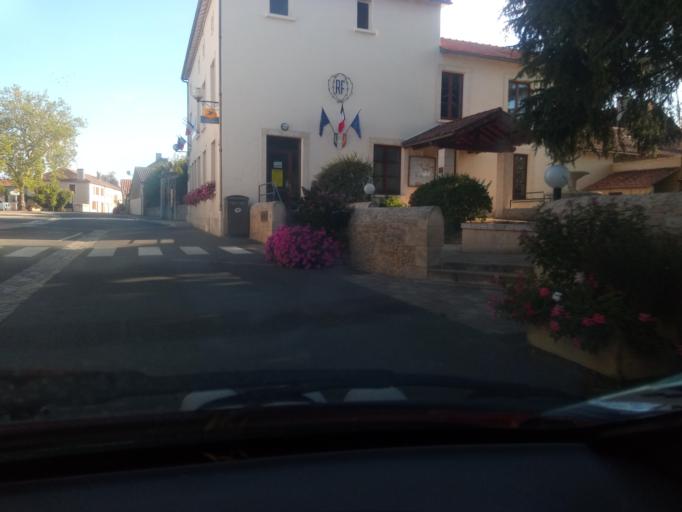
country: FR
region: Poitou-Charentes
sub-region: Departement de la Vienne
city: Lussac-les-Chateaux
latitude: 46.3435
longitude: 0.7051
